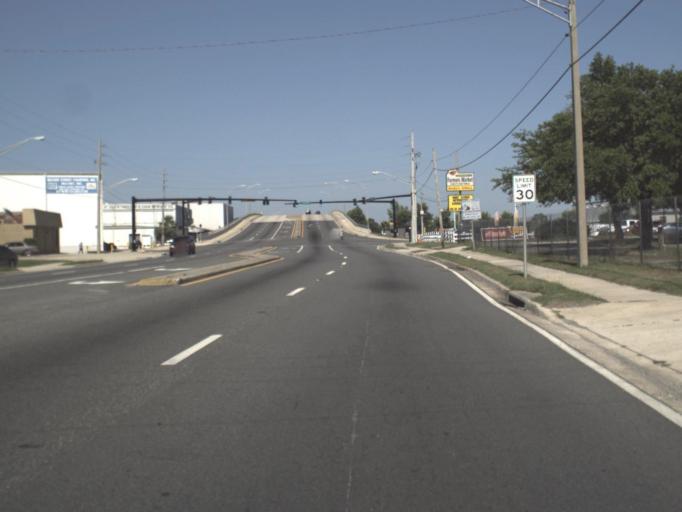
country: US
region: Florida
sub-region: Duval County
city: Jacksonville
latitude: 30.3342
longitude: -81.6898
